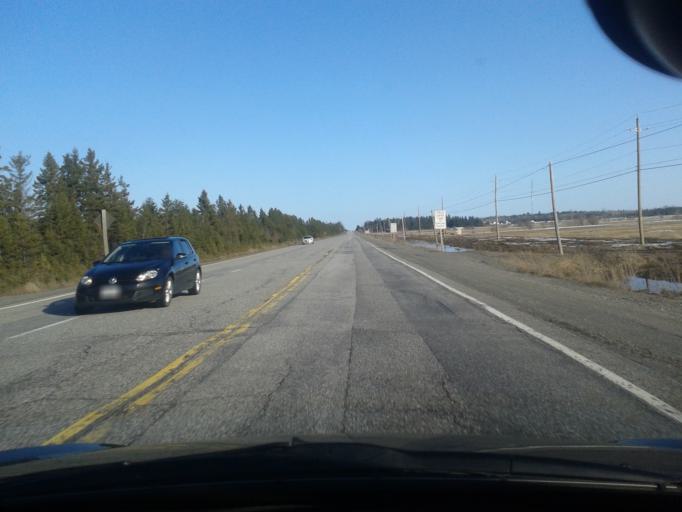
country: CA
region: Ontario
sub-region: Nipissing District
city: North Bay
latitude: 46.4035
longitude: -80.0302
